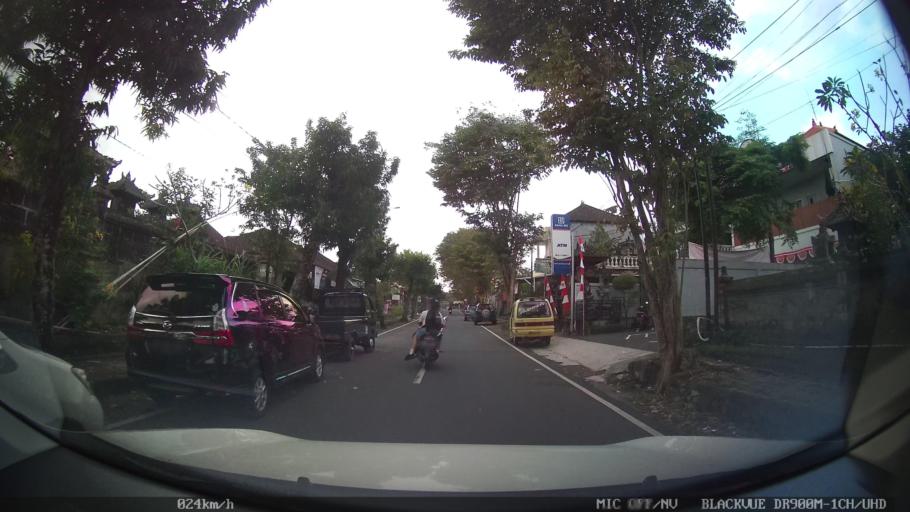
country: ID
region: Bali
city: Banjar Jambe Baleran
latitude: -8.5356
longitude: 115.1233
